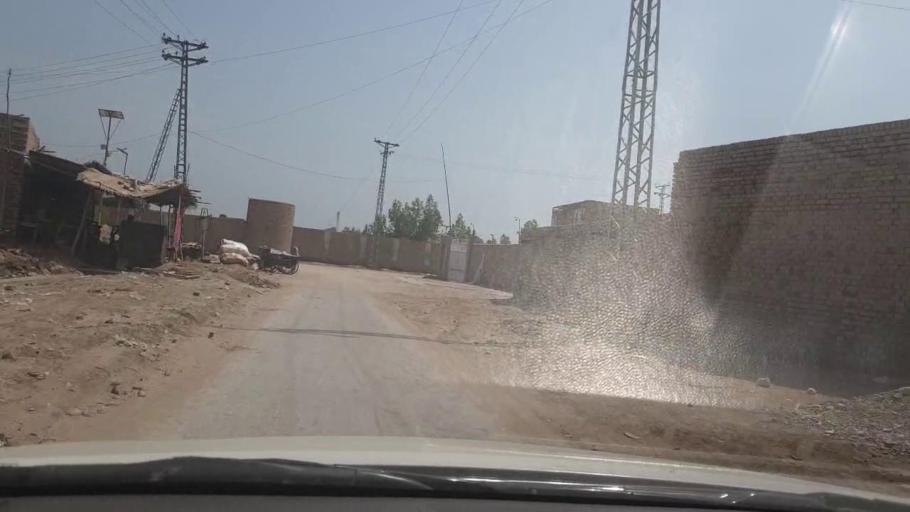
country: PK
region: Sindh
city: Garhi Yasin
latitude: 27.9113
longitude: 68.5112
